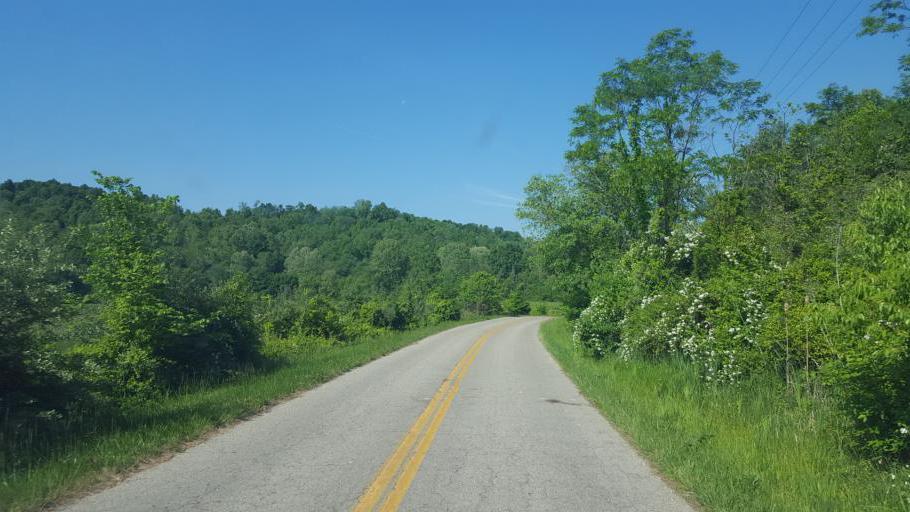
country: US
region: Ohio
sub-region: Jackson County
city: Wellston
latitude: 39.0117
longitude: -82.4586
